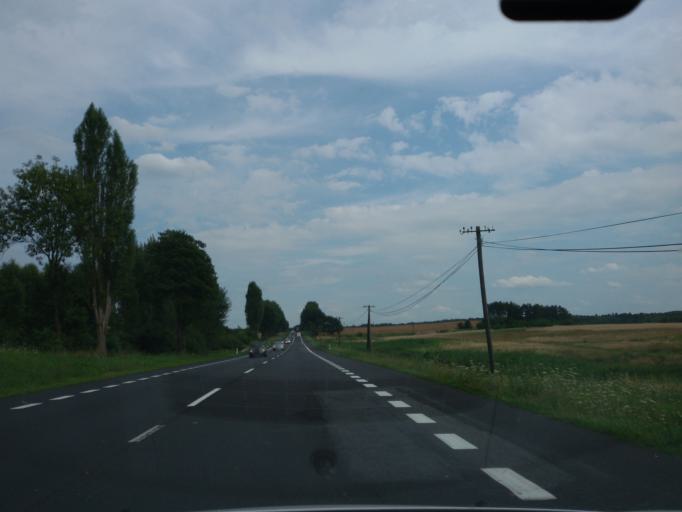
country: PL
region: Lubusz
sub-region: Powiat nowosolski
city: Nowe Miasteczko
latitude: 51.6757
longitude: 15.7836
